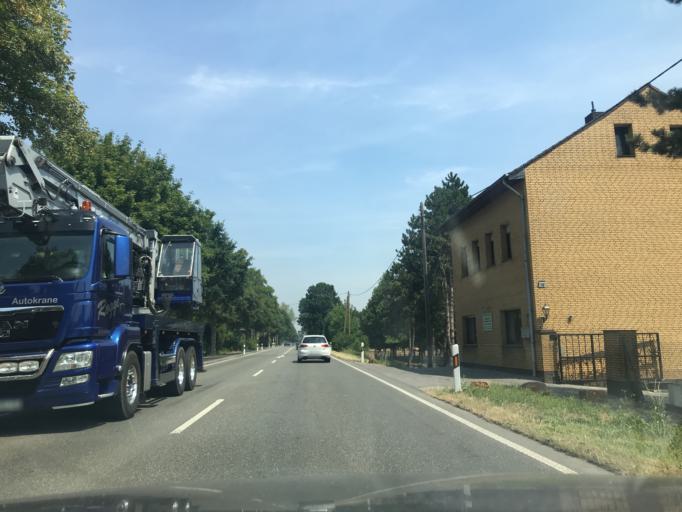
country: DE
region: North Rhine-Westphalia
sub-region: Regierungsbezirk Dusseldorf
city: Alpen
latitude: 51.5969
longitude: 6.5399
